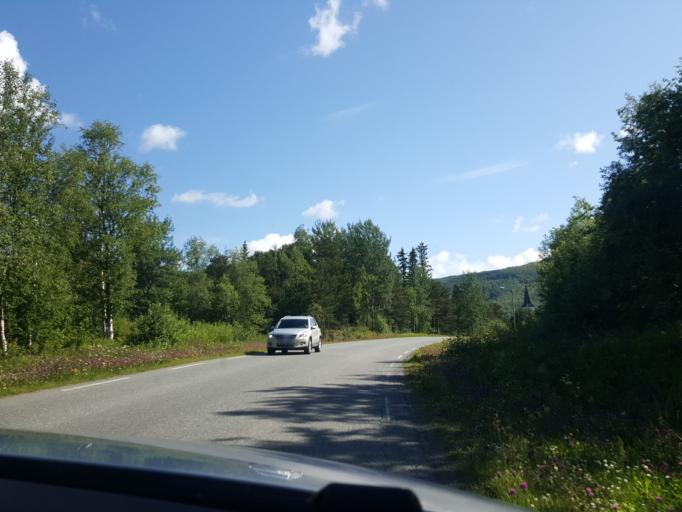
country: NO
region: Nordland
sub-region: Bodo
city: Loding
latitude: 67.1204
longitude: 14.9908
